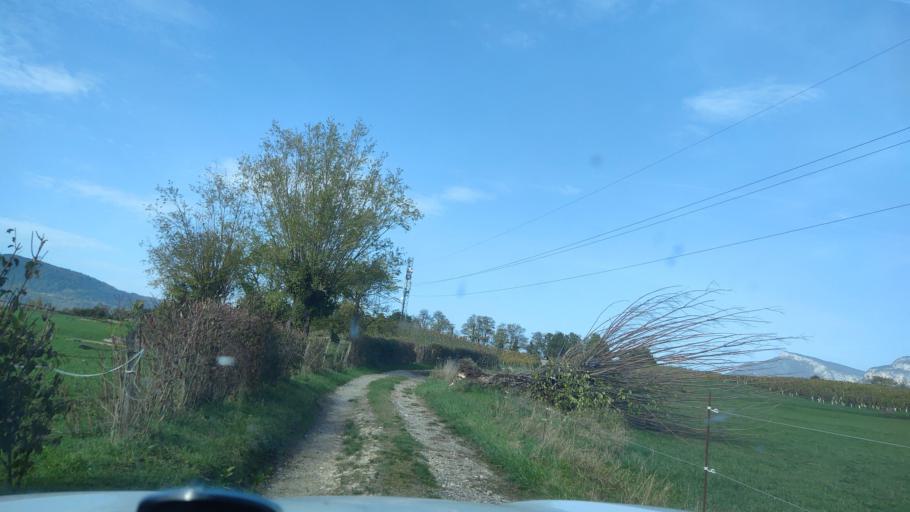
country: FR
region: Rhone-Alpes
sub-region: Departement de la Savoie
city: Les Marches
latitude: 45.5095
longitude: 5.9979
